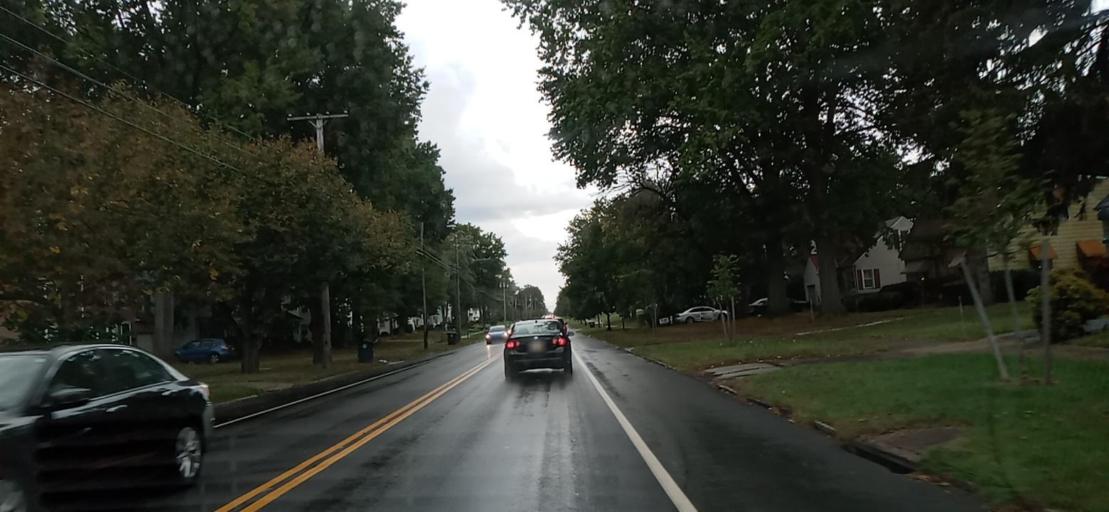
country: US
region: Ohio
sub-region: Summit County
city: Akron
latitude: 41.0876
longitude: -81.5694
